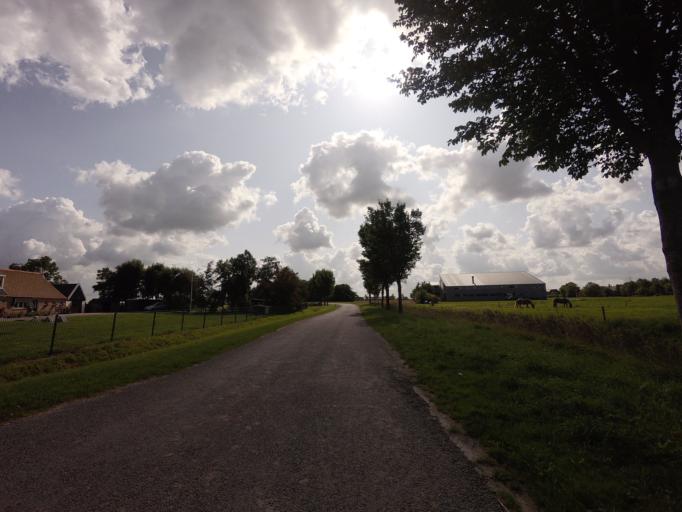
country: NL
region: Friesland
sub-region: Gemeente Het Bildt
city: Minnertsga
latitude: 53.2585
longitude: 5.6006
